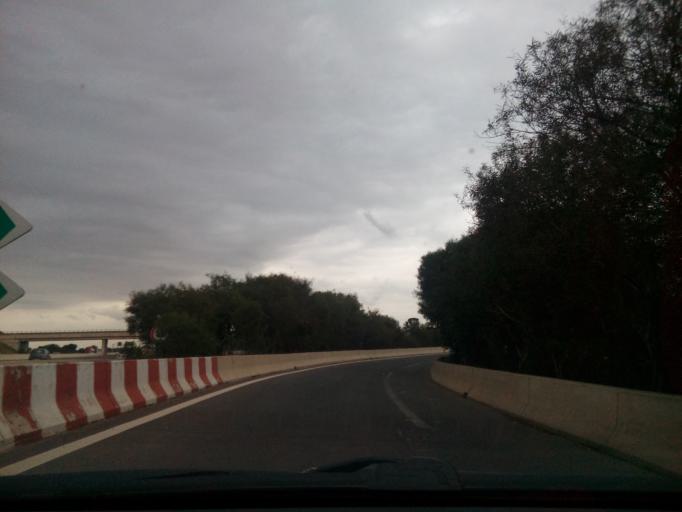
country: DZ
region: Mascara
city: Sig
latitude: 35.5819
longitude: -0.2228
